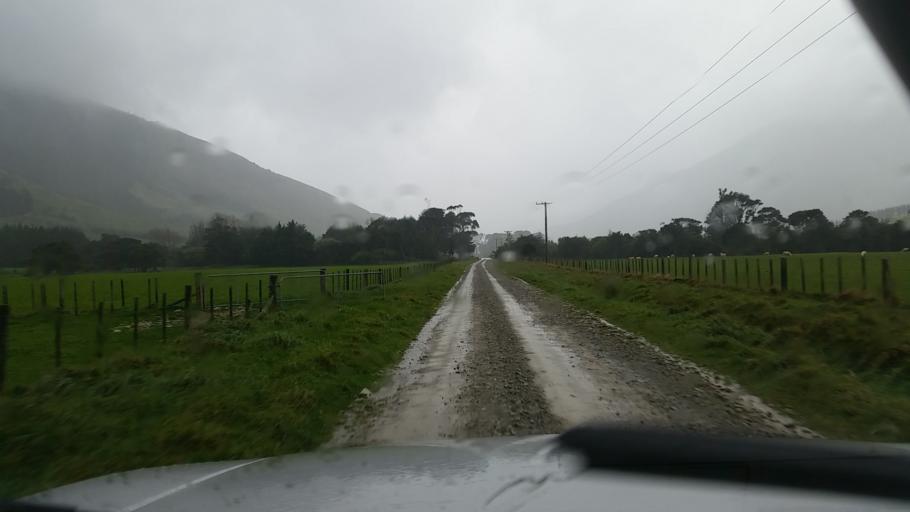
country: NZ
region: Marlborough
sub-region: Marlborough District
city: Picton
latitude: -41.1241
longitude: 174.0390
